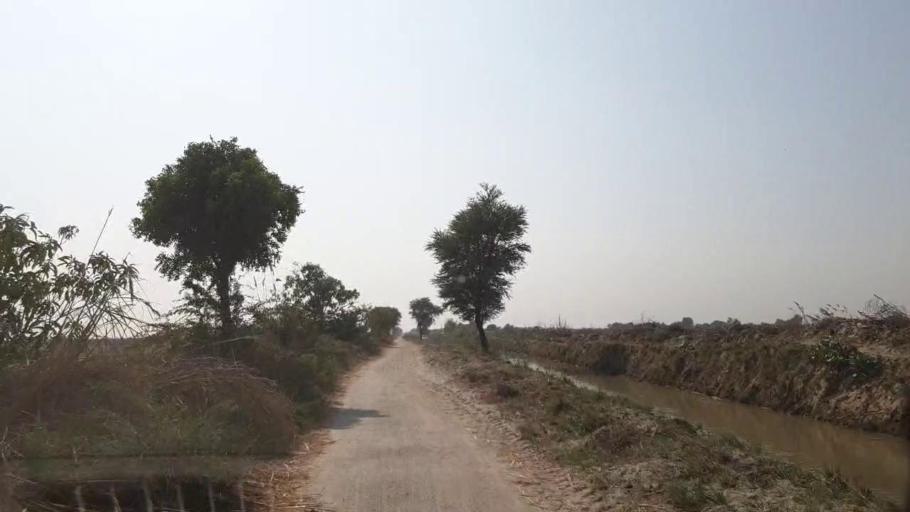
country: PK
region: Sindh
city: Bulri
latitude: 24.9642
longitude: 68.3921
